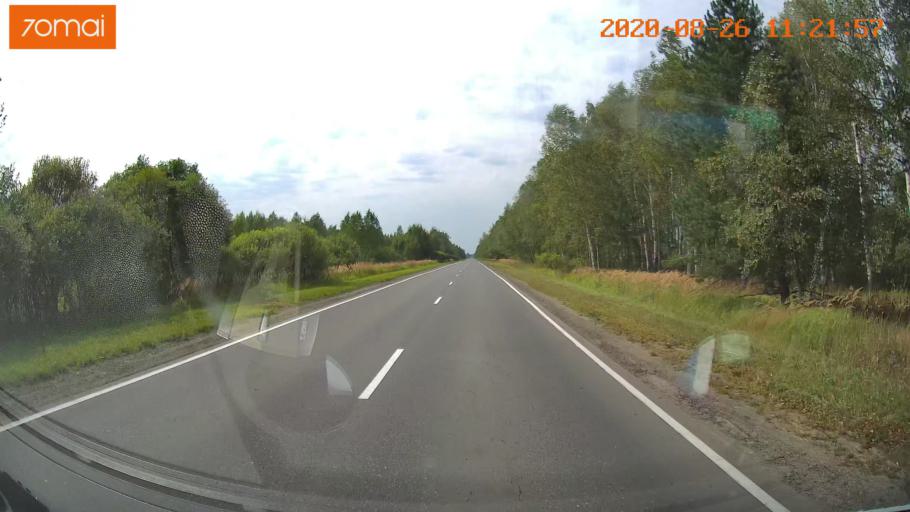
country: RU
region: Rjazan
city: Shilovo
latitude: 54.3702
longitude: 41.0358
